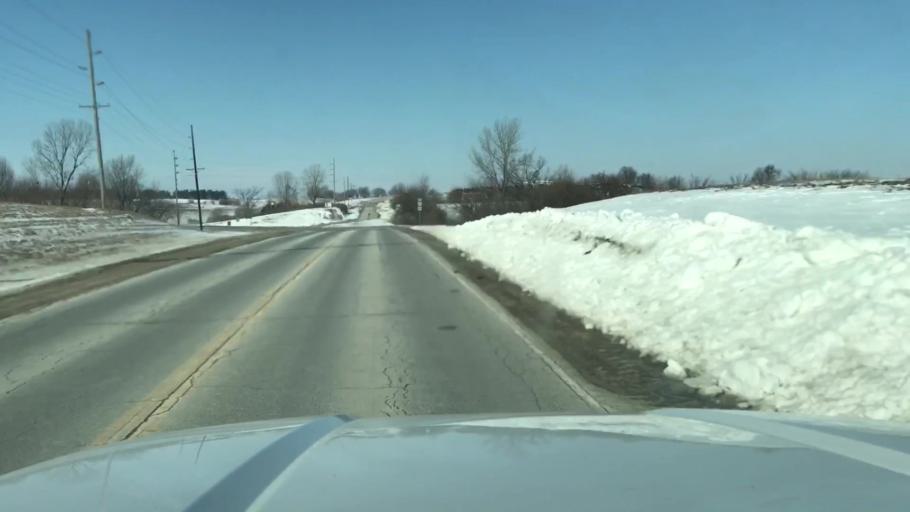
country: US
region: Missouri
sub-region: Andrew County
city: Savannah
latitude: 39.9609
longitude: -94.8562
